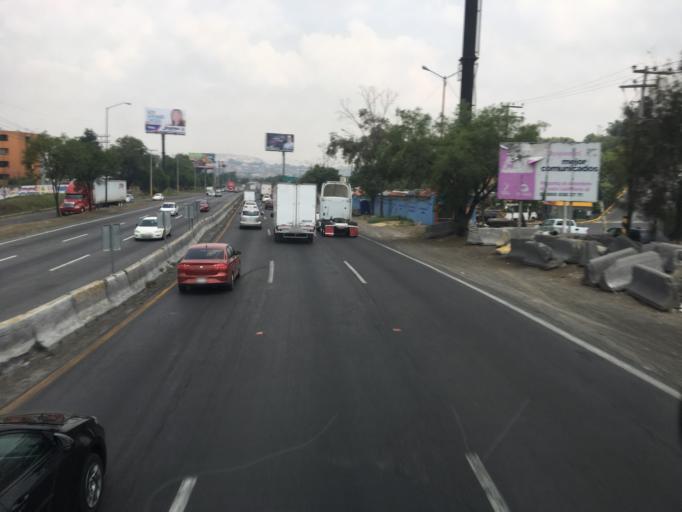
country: MX
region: Mexico
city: Tlalnepantla
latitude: 19.5593
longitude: -99.1868
